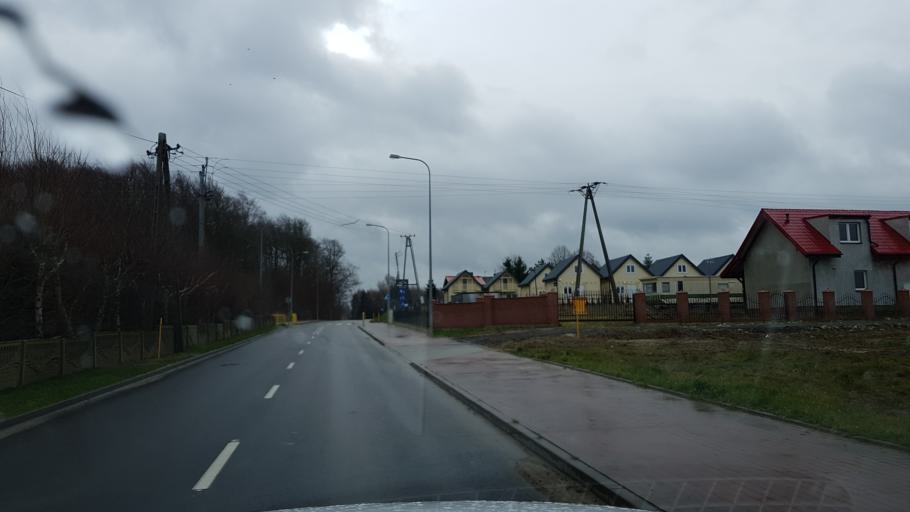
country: PL
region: West Pomeranian Voivodeship
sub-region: Powiat kolobrzeski
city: Ustronie Morskie
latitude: 54.2083
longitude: 15.7664
